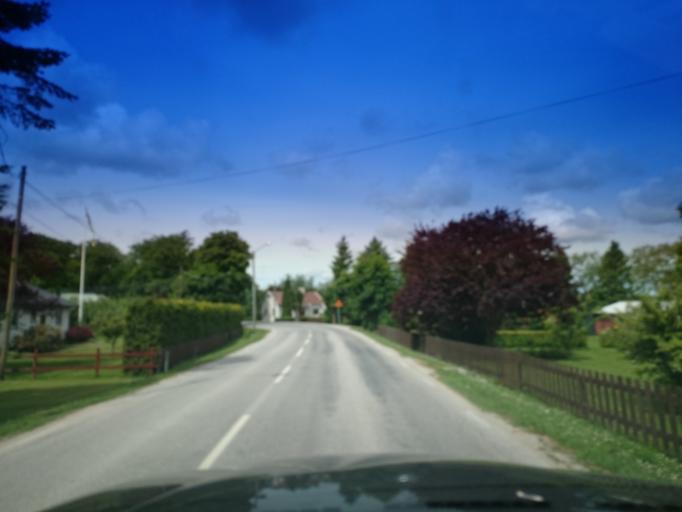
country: SE
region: Gotland
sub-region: Gotland
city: Hemse
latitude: 57.2576
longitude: 18.6325
